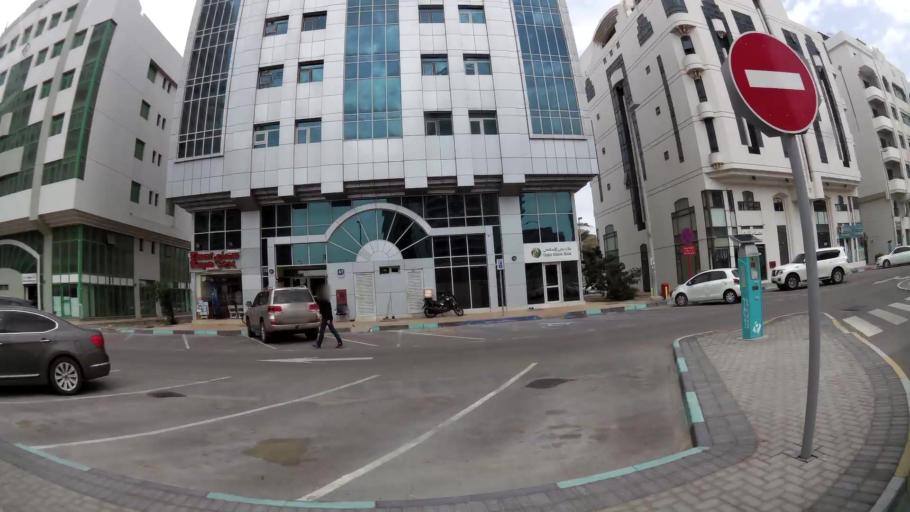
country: AE
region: Abu Dhabi
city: Abu Dhabi
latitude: 24.4321
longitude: 54.4364
